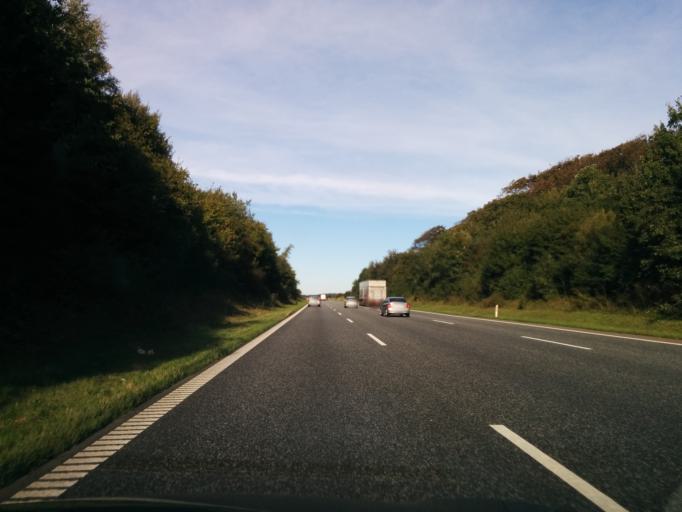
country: DK
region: South Denmark
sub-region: Fredericia Kommune
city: Taulov
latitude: 55.6056
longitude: 9.5853
